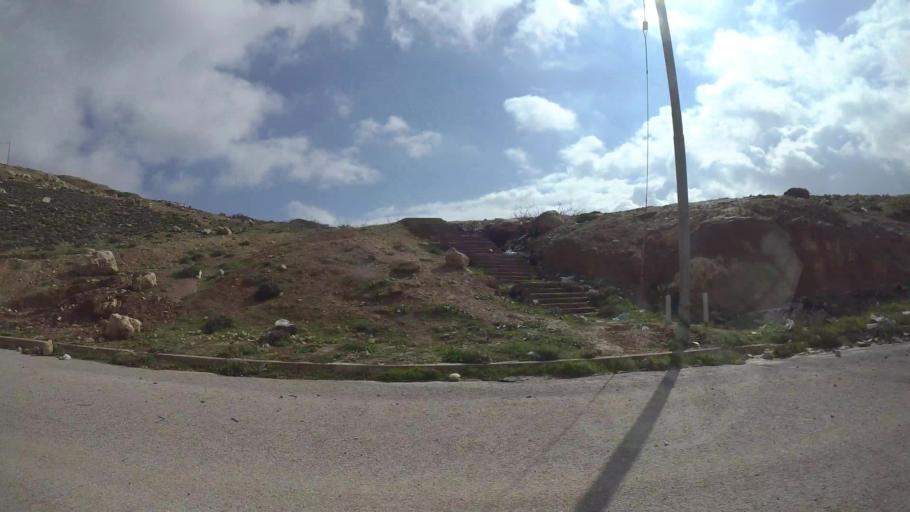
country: JO
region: Amman
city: Al Jubayhah
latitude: 32.0577
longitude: 35.8630
